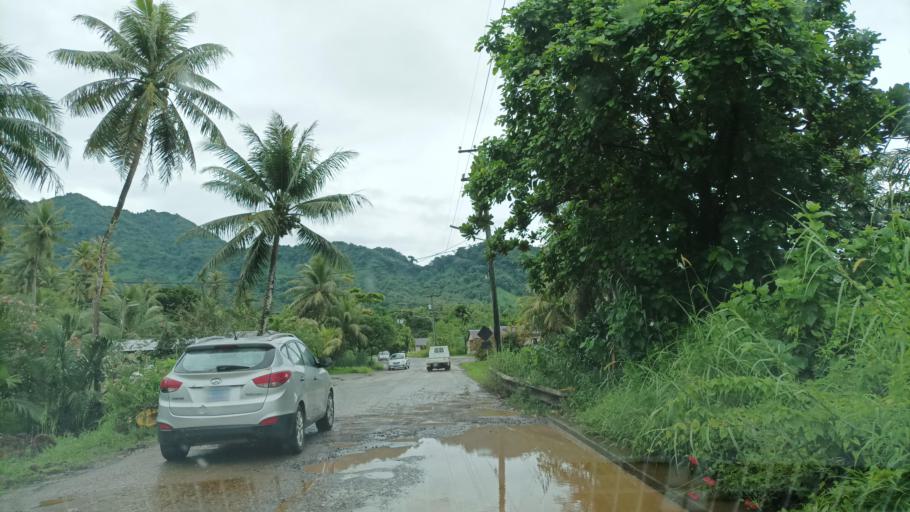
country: FM
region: Kosrae
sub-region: Lelu Municipality
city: Tofol
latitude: 5.3273
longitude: 163.0085
